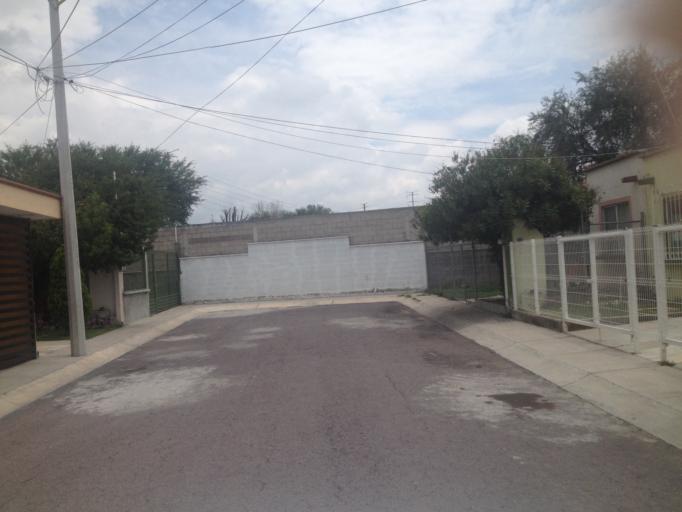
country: MX
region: Aguascalientes
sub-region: Aguascalientes
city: San Sebastian [Fraccionamiento]
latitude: 21.8207
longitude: -102.2685
